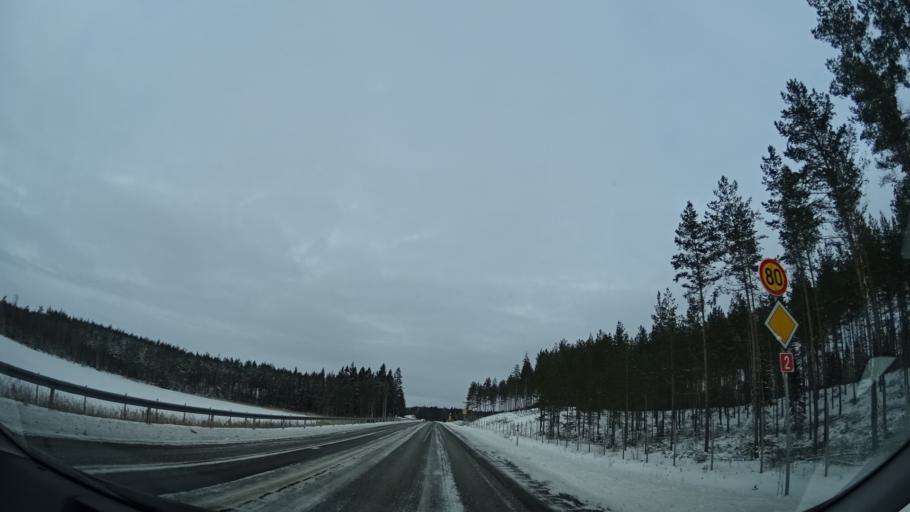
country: FI
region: Uusimaa
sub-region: Helsinki
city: Kaerkoelae
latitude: 60.6141
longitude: 24.0291
